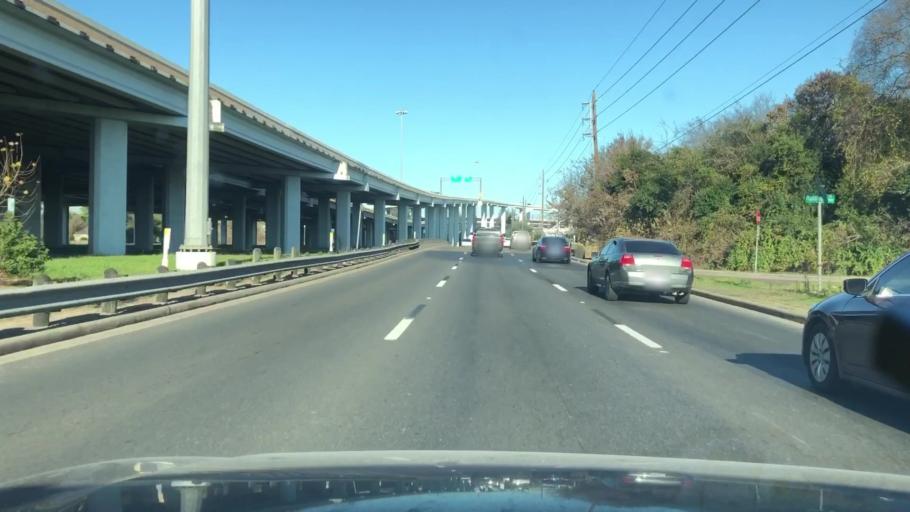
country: US
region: Texas
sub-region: Fort Bend County
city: Meadows Place
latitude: 29.6560
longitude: -95.5523
